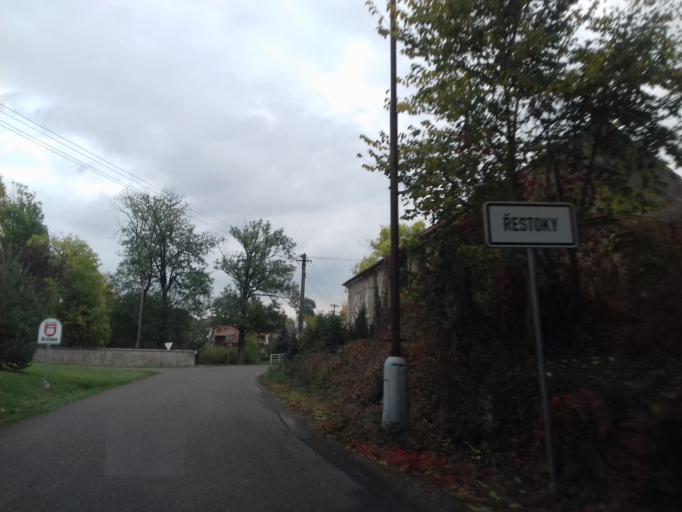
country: CZ
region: Pardubicky
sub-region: Okres Chrudim
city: Chrast
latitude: 49.9207
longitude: 15.9111
